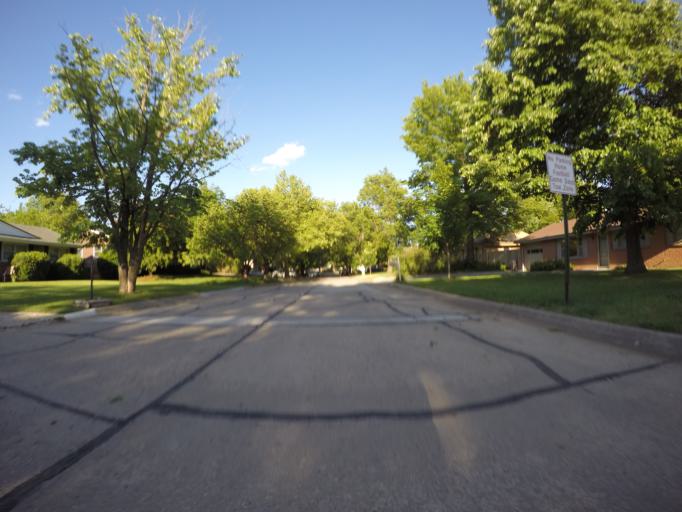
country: US
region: Kansas
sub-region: Riley County
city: Manhattan
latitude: 39.2028
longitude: -96.6036
